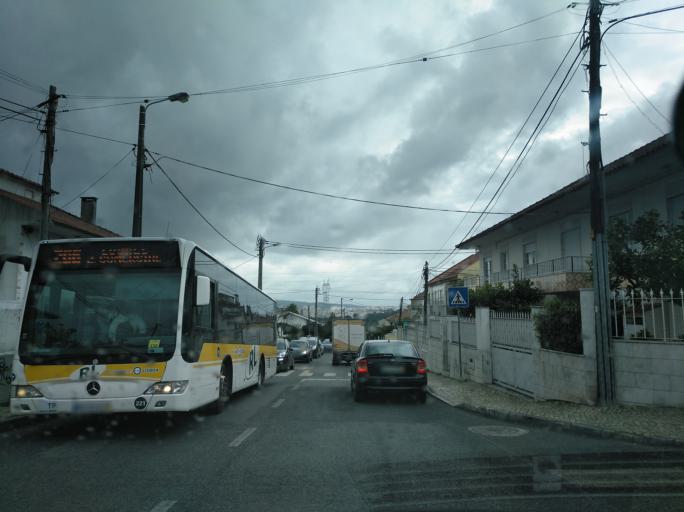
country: PT
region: Lisbon
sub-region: Odivelas
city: Famoes
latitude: 38.7883
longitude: -9.2093
